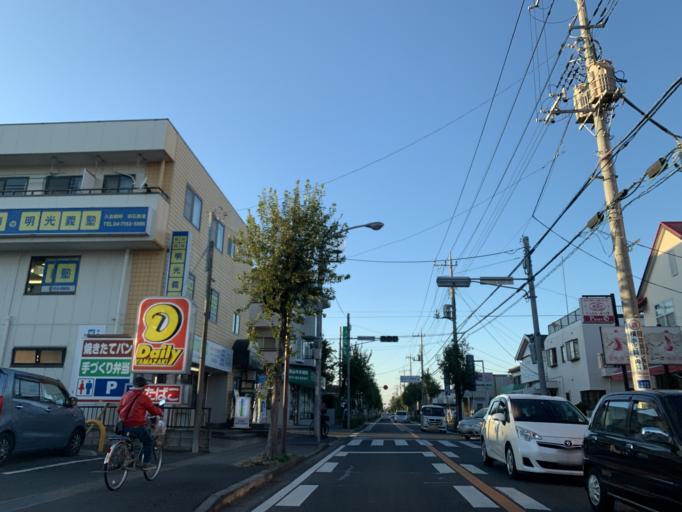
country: JP
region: Chiba
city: Nagareyama
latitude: 35.8876
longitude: 139.9189
